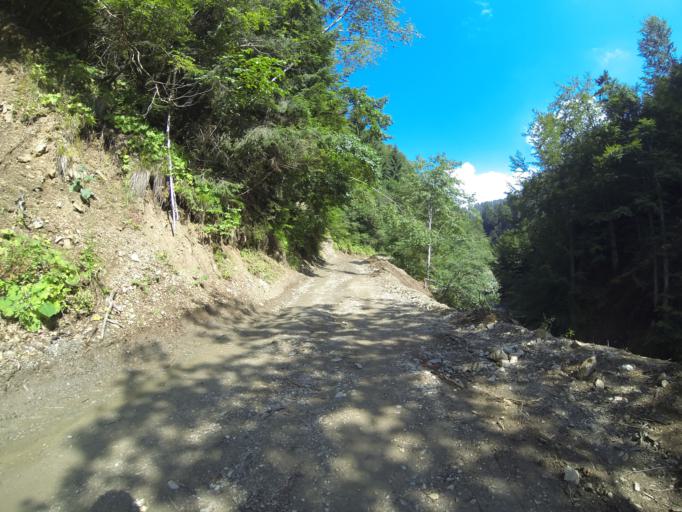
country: RO
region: Valcea
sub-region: Comuna Costesti
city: Bistrita
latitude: 45.2514
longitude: 23.9915
